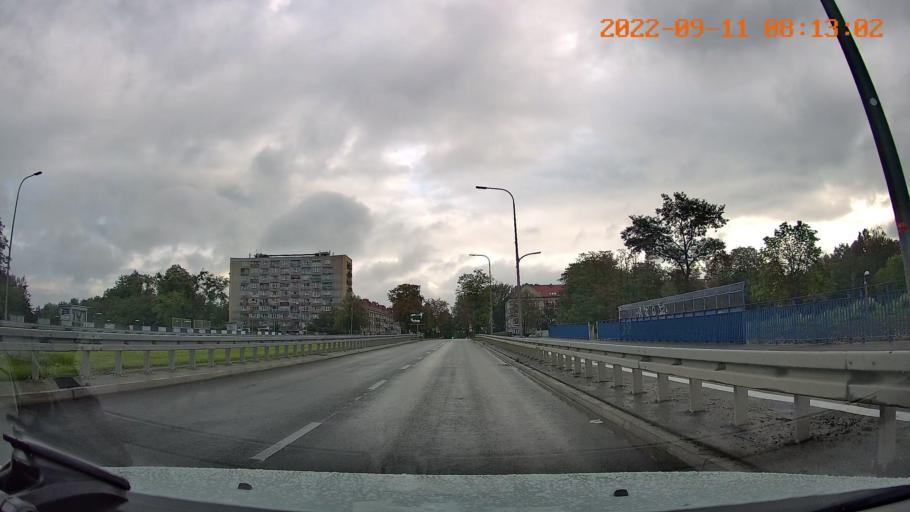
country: PL
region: Silesian Voivodeship
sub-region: Tychy
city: Tychy
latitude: 50.1169
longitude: 18.9825
